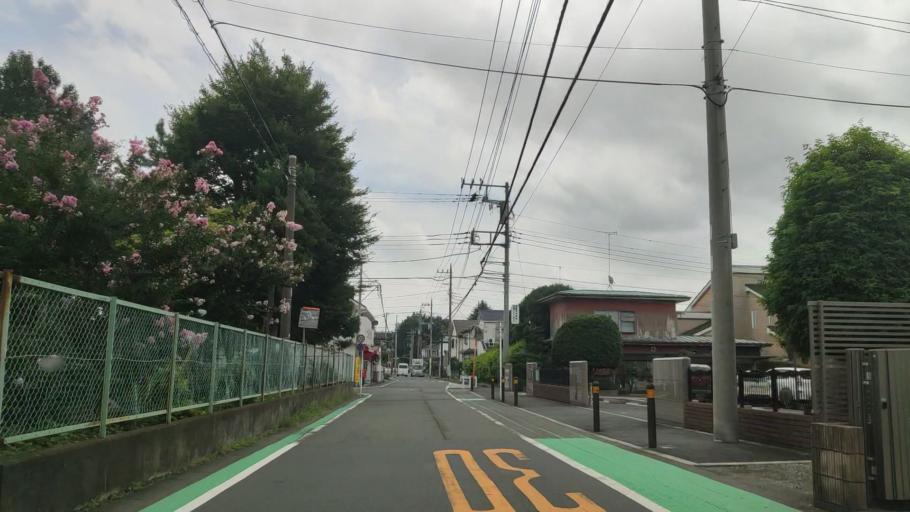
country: JP
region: Tokyo
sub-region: Machida-shi
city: Machida
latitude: 35.5183
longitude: 139.4444
